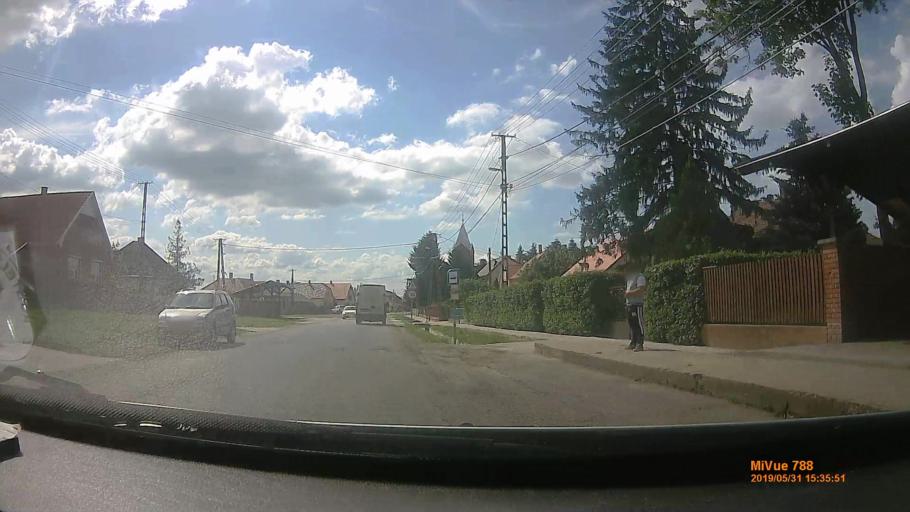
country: HU
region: Borsod-Abauj-Zemplen
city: Prugy
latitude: 48.0812
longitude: 21.2420
